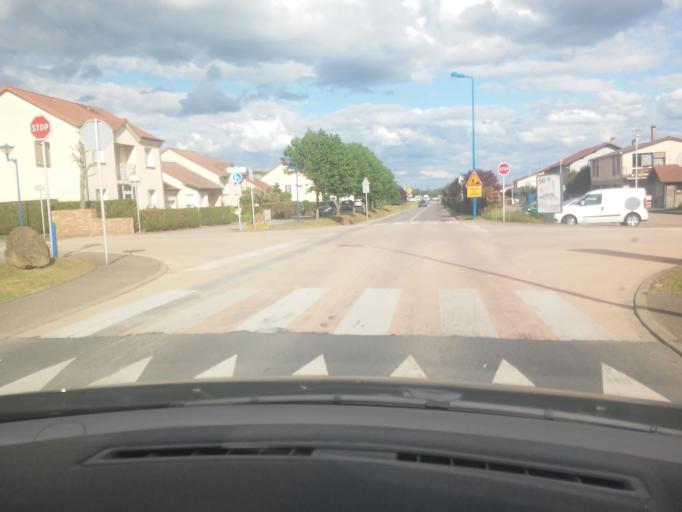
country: FR
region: Lorraine
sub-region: Departement de la Moselle
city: Marange-Silvange
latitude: 49.2119
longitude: 6.1188
